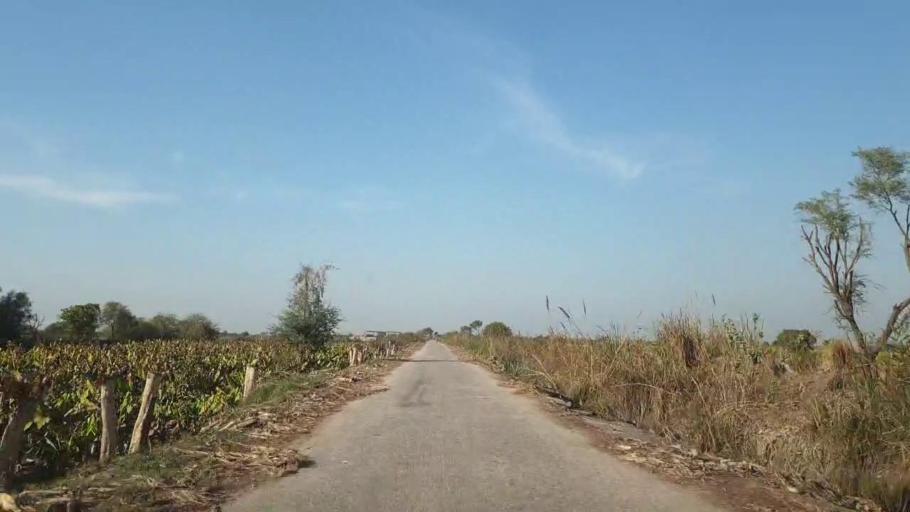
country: PK
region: Sindh
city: Tando Adam
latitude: 25.7254
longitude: 68.7028
